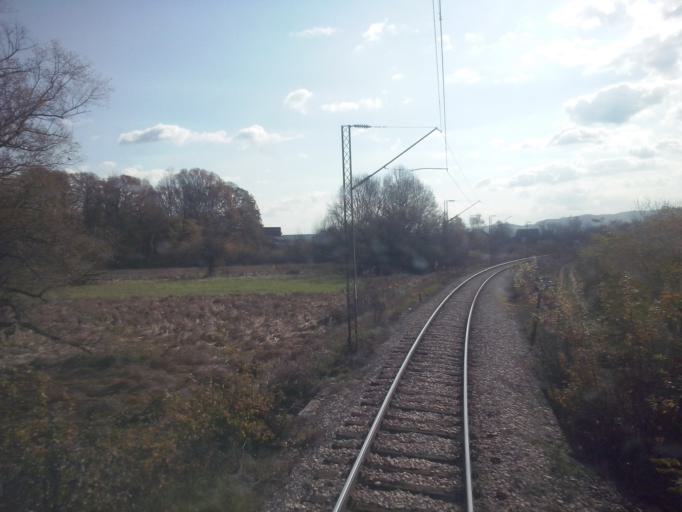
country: RS
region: Central Serbia
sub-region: Zlatiborski Okrug
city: Pozega
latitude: 43.8622
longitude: 20.0146
